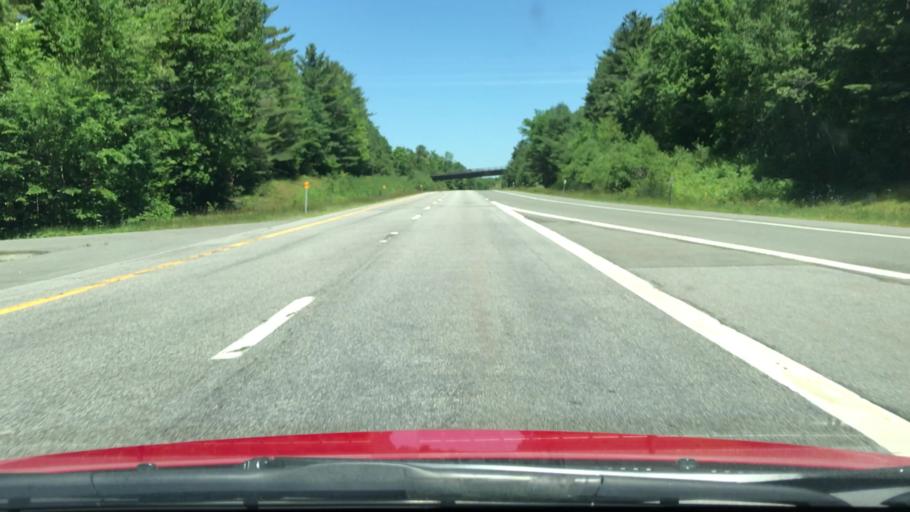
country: US
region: New York
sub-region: Essex County
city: Elizabethtown
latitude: 44.1647
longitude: -73.5836
